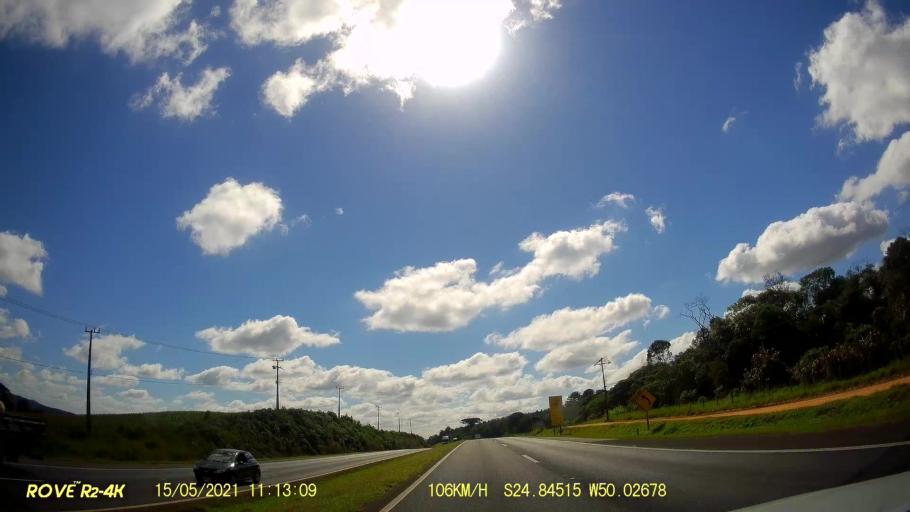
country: BR
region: Parana
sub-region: Castro
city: Castro
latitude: -24.8454
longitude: -50.0269
